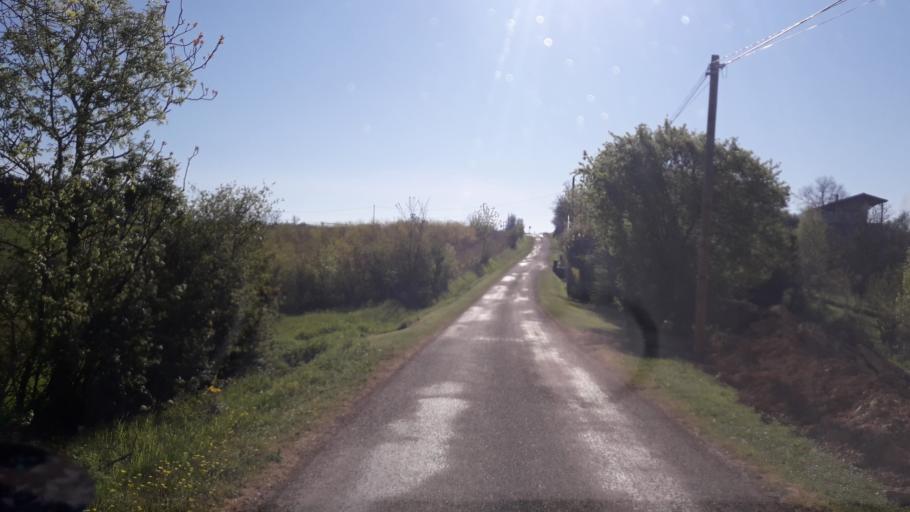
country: FR
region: Midi-Pyrenees
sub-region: Departement de la Haute-Garonne
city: Montesquieu-Volvestre
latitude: 43.2007
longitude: 1.2830
